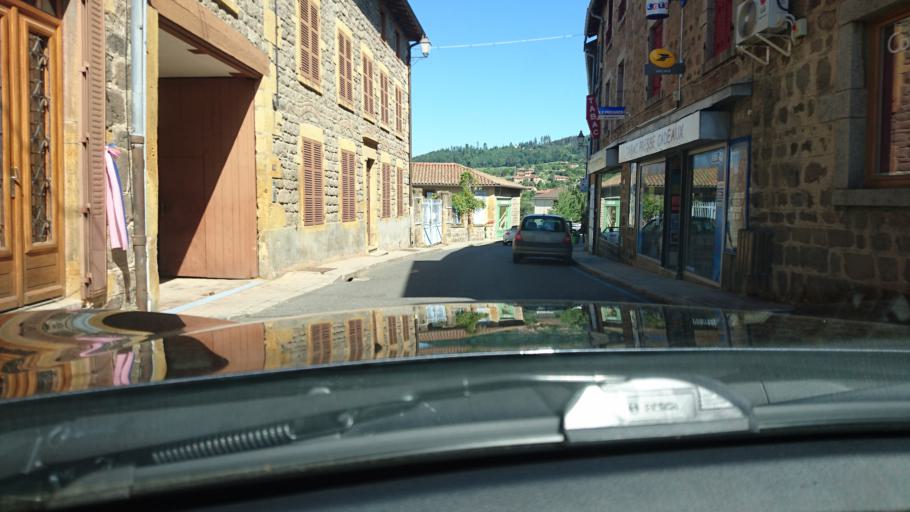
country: FR
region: Rhone-Alpes
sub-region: Departement du Rhone
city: Montrottier
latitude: 45.7903
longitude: 4.4660
